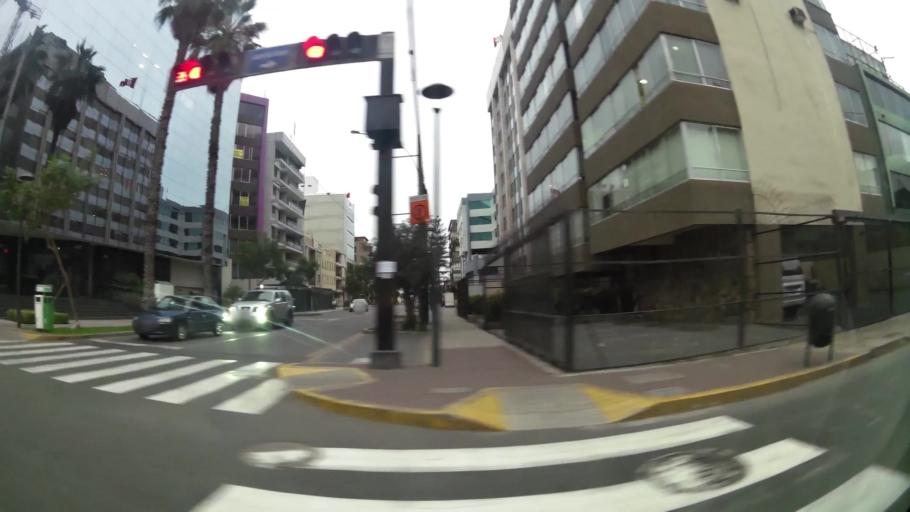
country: PE
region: Lima
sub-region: Lima
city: San Isidro
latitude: -12.0966
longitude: -77.0289
